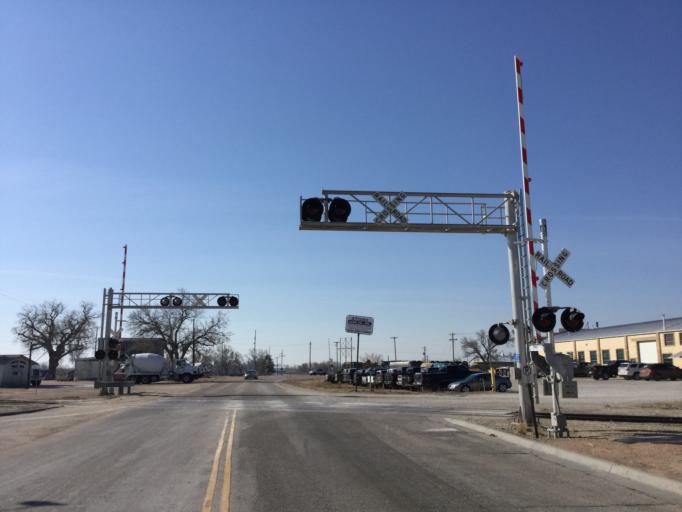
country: US
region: Kansas
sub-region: Barton County
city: Great Bend
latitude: 38.3562
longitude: -98.7742
